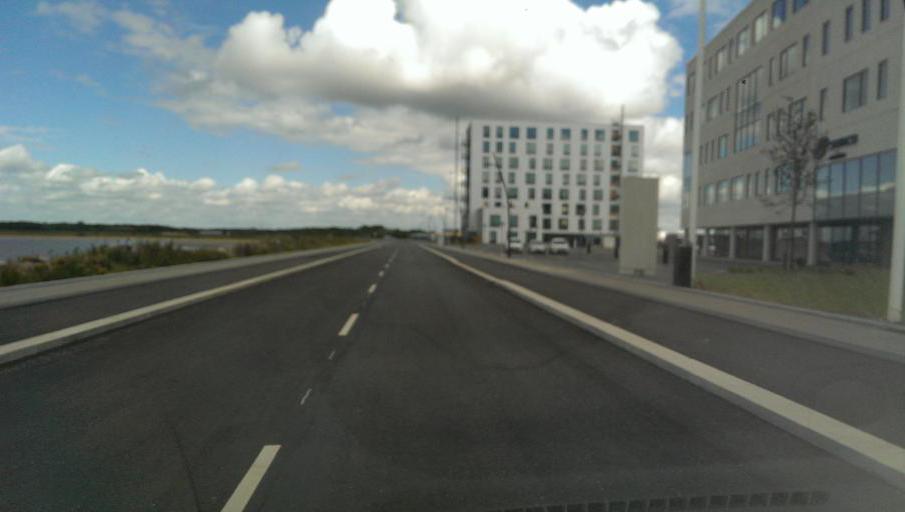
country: DK
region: South Denmark
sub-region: Fano Kommune
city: Nordby
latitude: 55.4804
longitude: 8.4095
